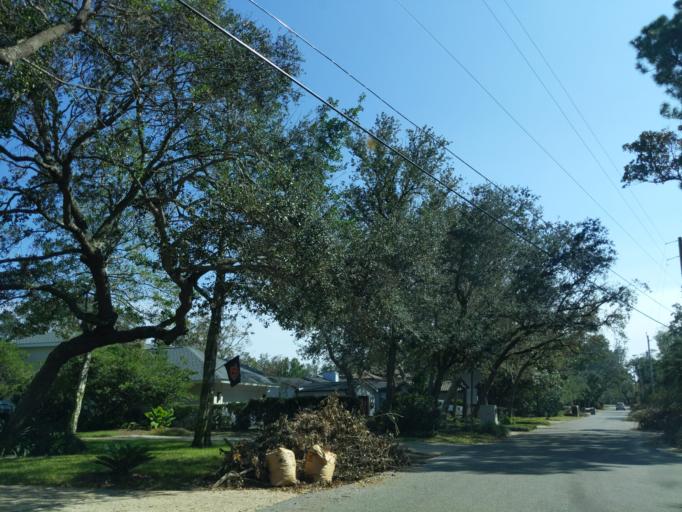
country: US
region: Florida
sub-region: Santa Rosa County
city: Gulf Breeze
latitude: 30.3634
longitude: -87.1812
